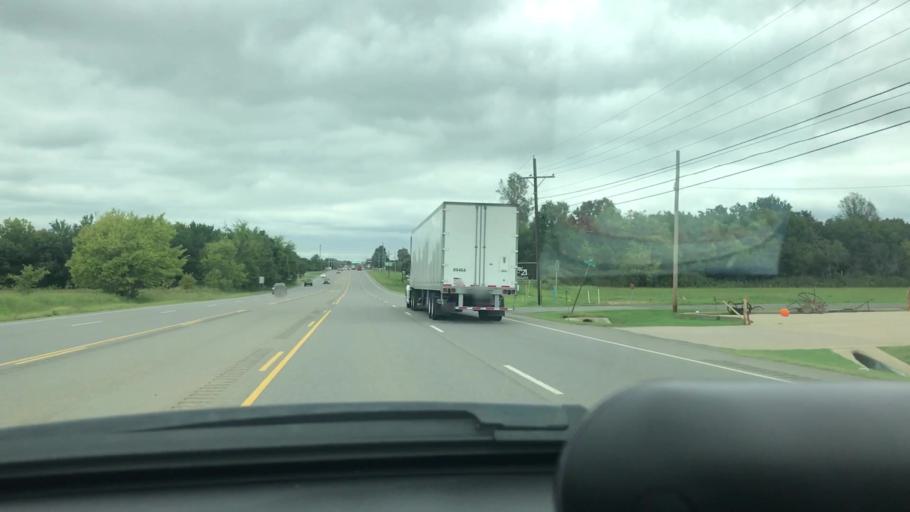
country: US
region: Oklahoma
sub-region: Wagoner County
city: Wagoner
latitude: 35.9387
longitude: -95.3952
